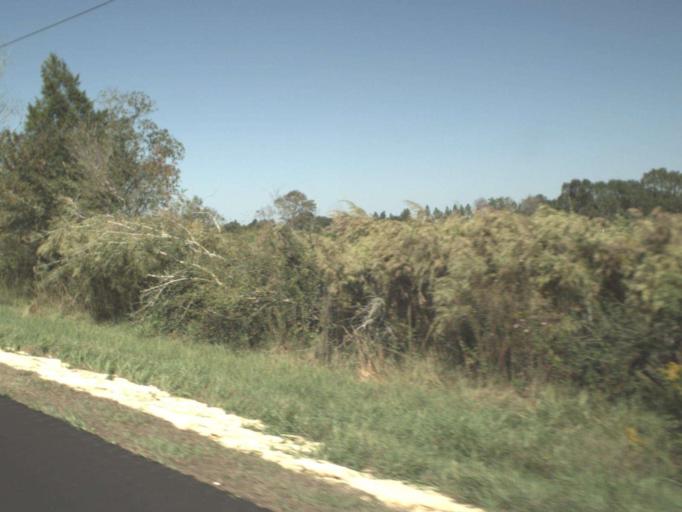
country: US
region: Alabama
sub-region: Covington County
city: Florala
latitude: 30.8798
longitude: -86.2686
